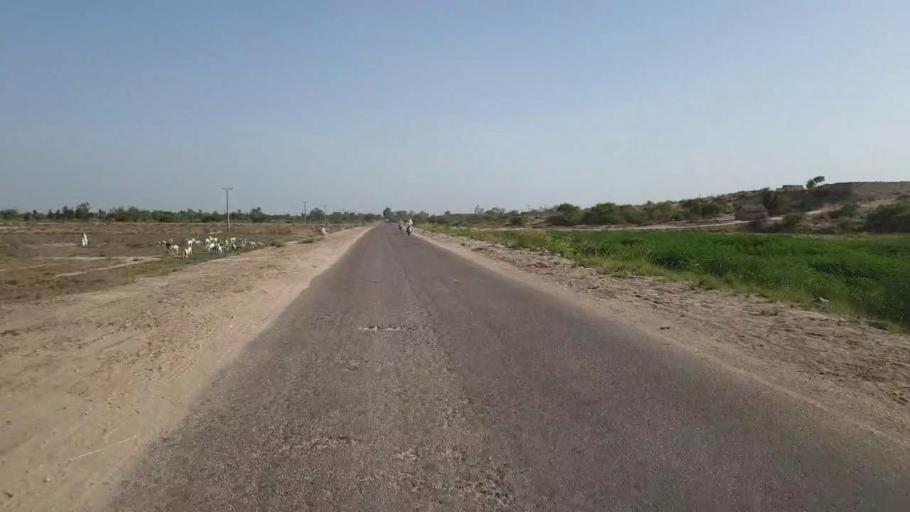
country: PK
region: Sindh
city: Daur
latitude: 26.4697
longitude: 68.4531
